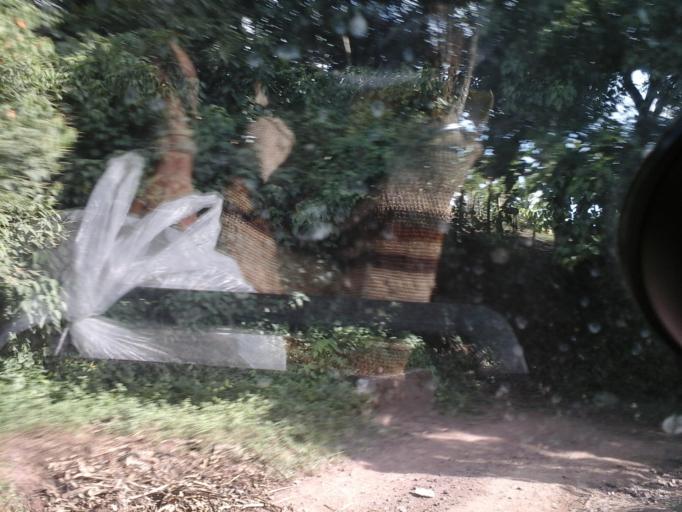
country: CO
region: Cesar
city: San Diego
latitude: 10.2556
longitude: -73.1098
